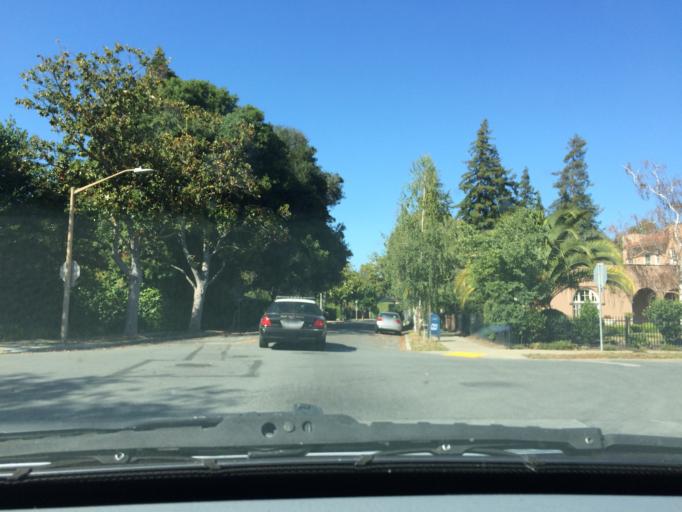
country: US
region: California
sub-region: Santa Clara County
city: Palo Alto
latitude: 37.4534
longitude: -122.1520
